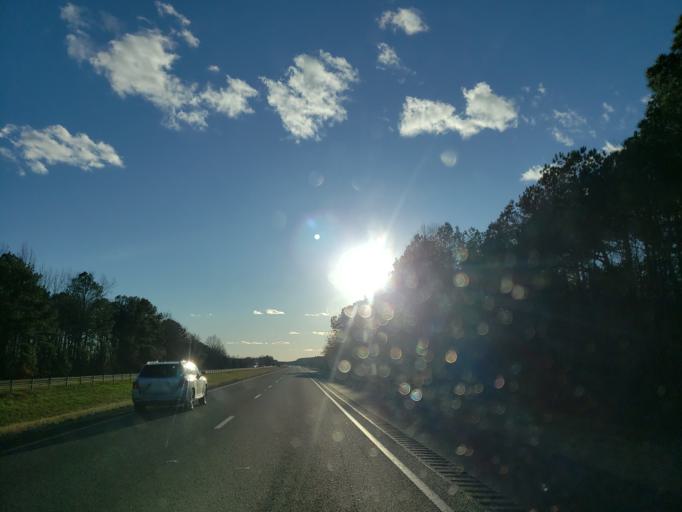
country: US
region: Alabama
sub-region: Sumter County
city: Livingston
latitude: 32.7218
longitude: -88.1188
